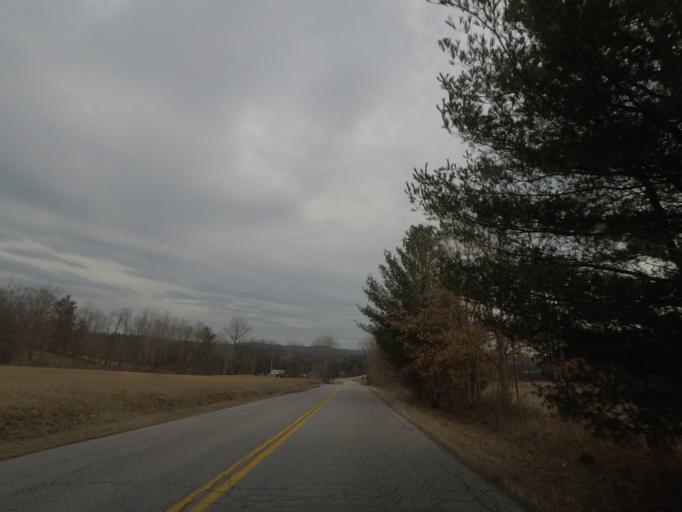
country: US
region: New York
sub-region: Rensselaer County
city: Hoosick Falls
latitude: 42.8870
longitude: -73.4425
